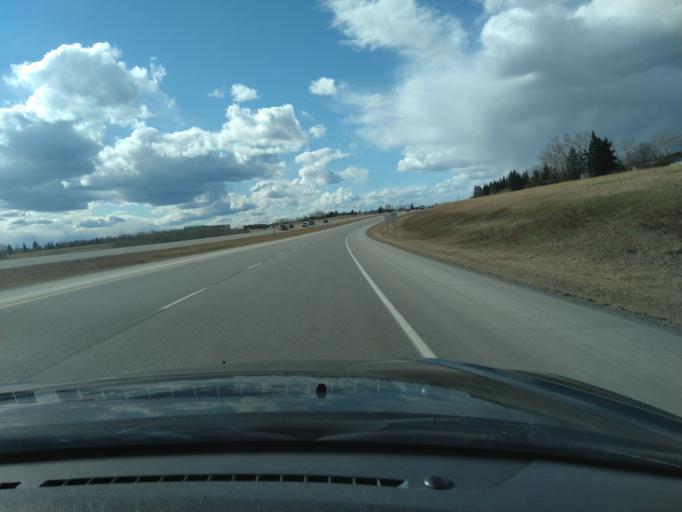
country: CA
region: Alberta
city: Cochrane
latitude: 51.1488
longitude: -114.2698
